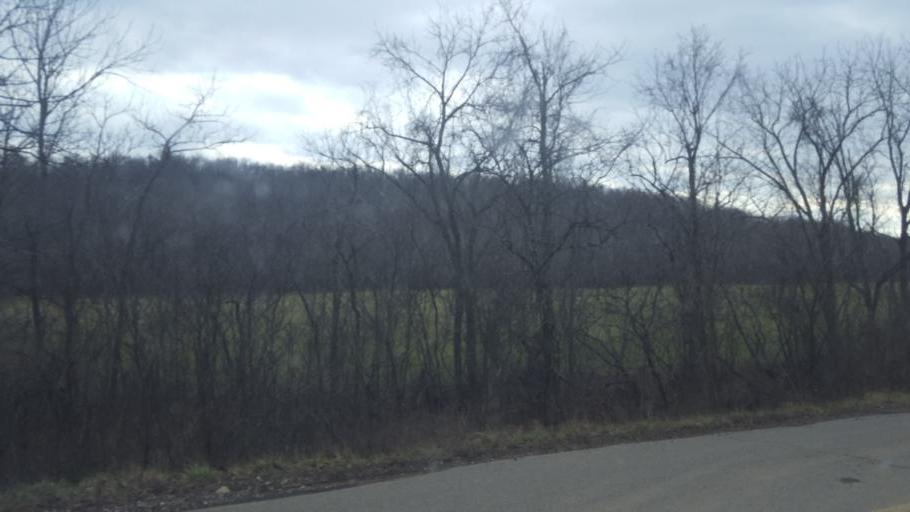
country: US
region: Ohio
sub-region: Gallia County
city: Gallipolis
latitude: 38.7317
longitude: -82.3172
